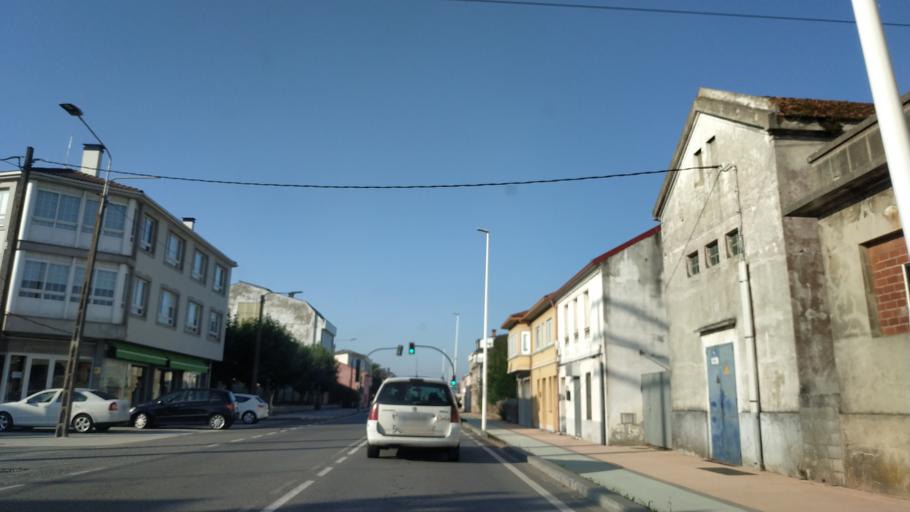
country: ES
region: Galicia
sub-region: Provincia da Coruna
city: Carballo
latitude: 43.2261
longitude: -8.6785
